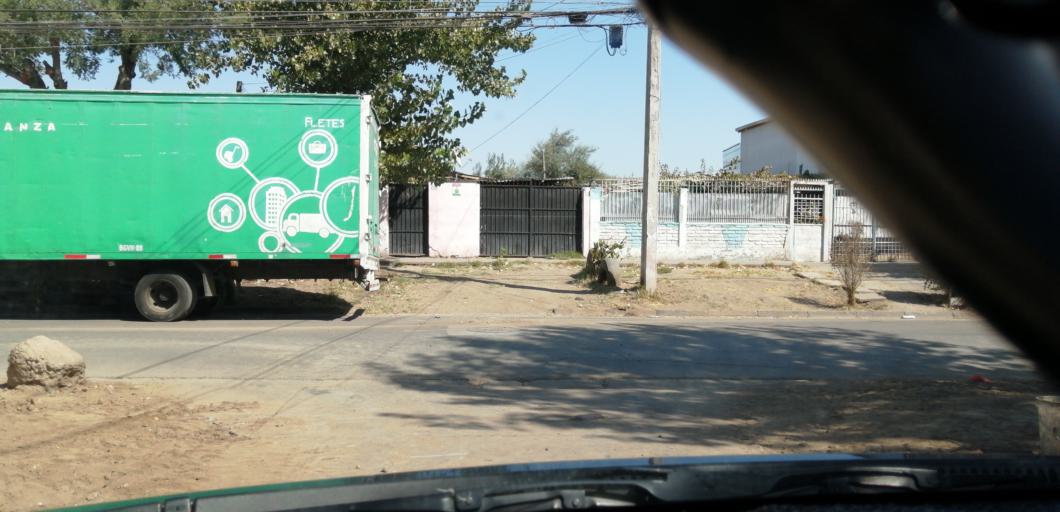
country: CL
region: Santiago Metropolitan
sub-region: Provincia de Santiago
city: Lo Prado
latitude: -33.4423
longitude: -70.7424
